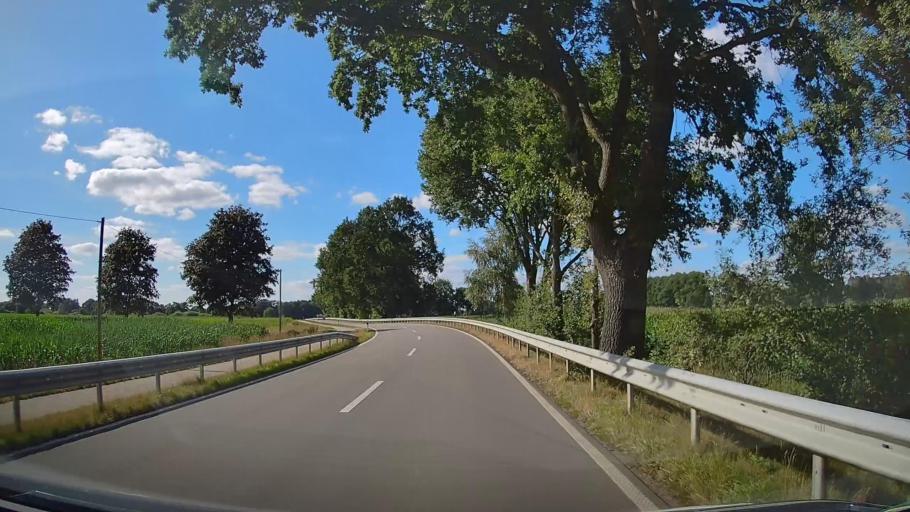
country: DE
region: Lower Saxony
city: Menslage
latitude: 52.6889
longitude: 7.7728
